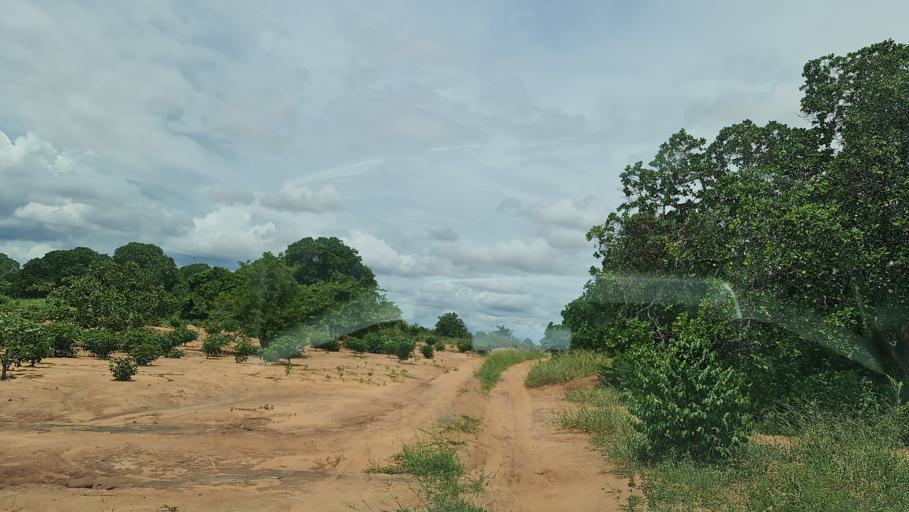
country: MZ
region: Nampula
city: Nacala
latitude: -14.7906
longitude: 39.9674
